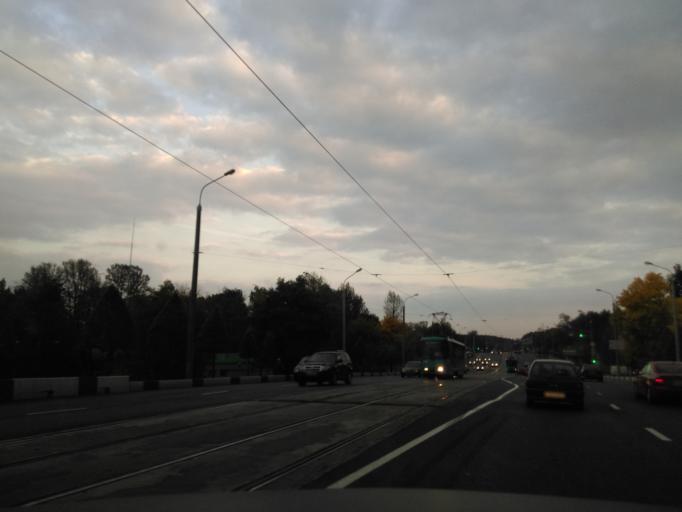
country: BY
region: Minsk
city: Minsk
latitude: 53.8930
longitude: 27.6110
